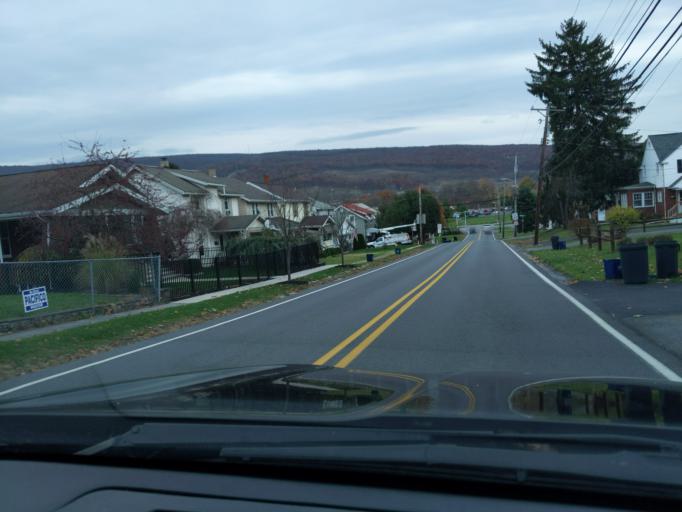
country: US
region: Pennsylvania
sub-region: Blair County
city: Altoona
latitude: 40.4982
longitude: -78.3955
